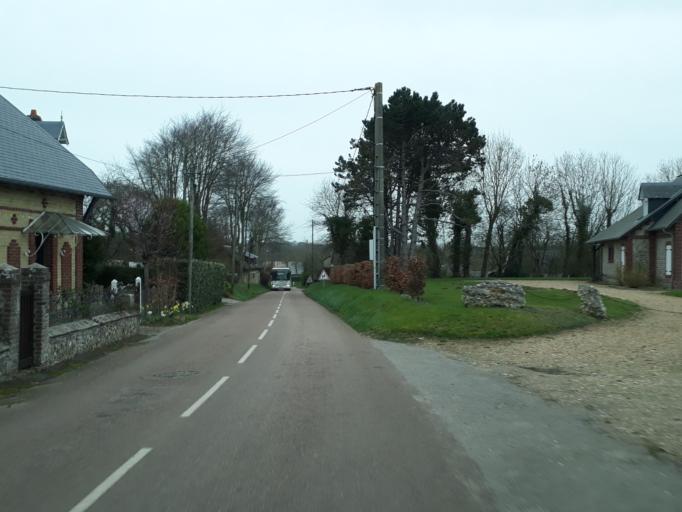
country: FR
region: Haute-Normandie
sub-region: Departement de la Seine-Maritime
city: Les Loges
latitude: 49.7294
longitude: 0.2841
